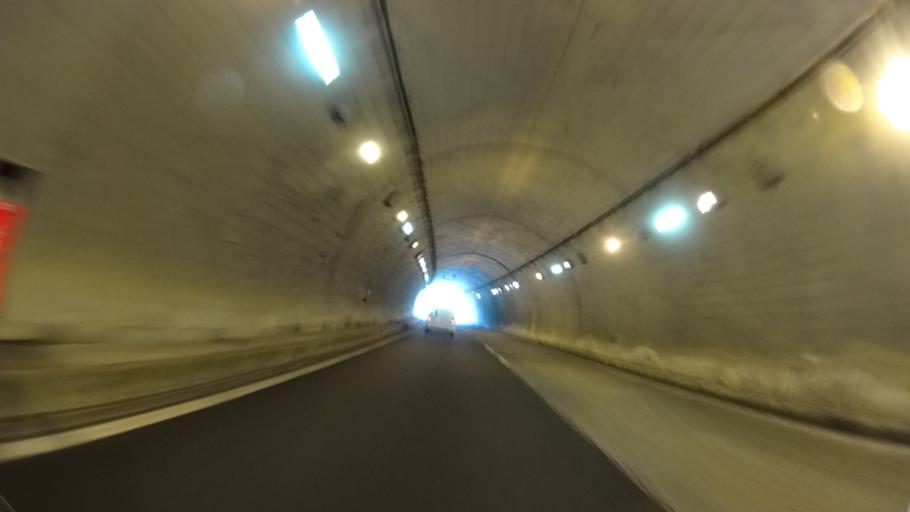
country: JP
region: Kumamoto
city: Yatsushiro
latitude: 32.4358
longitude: 130.6871
